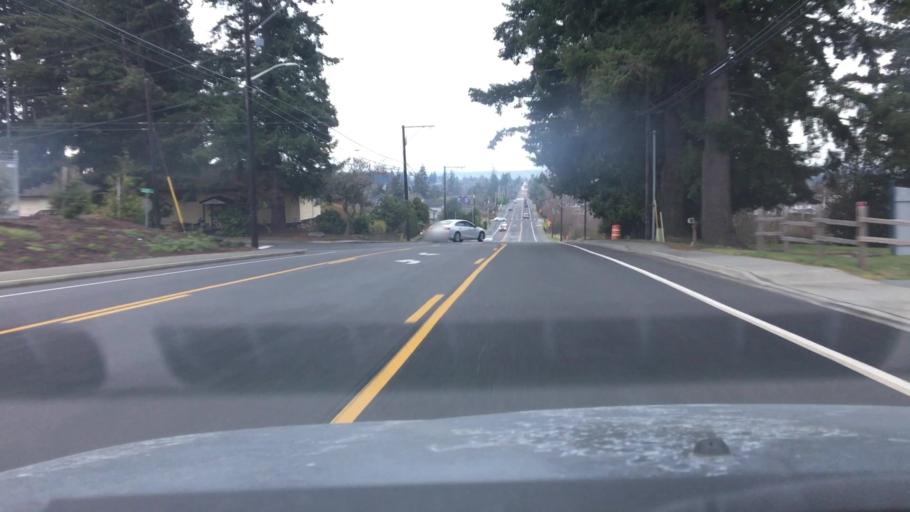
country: US
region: Washington
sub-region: Skagit County
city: Mount Vernon
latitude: 48.4209
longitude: -122.2966
